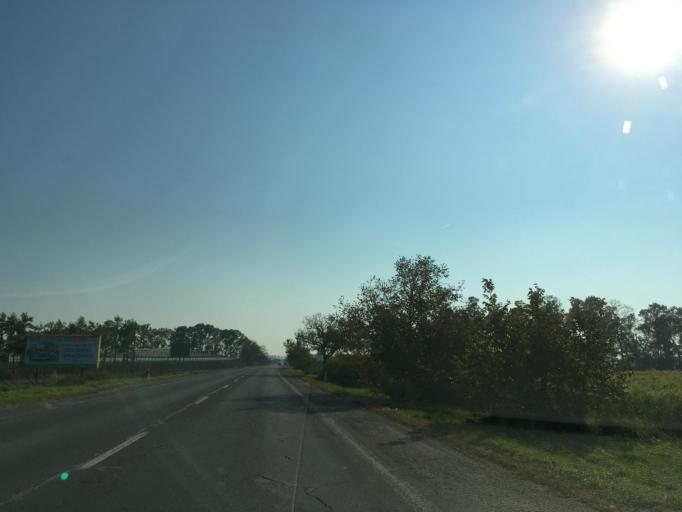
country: SK
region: Bratislavsky
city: Dunajska Luzna
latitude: 48.0714
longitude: 17.2747
